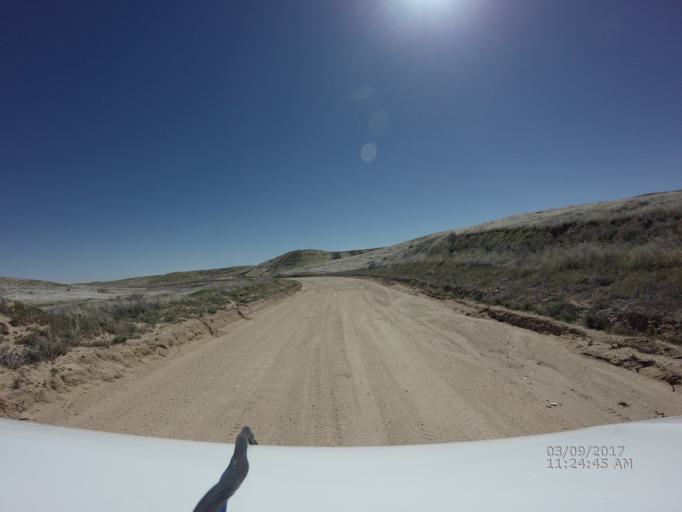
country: US
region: California
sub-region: Los Angeles County
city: Green Valley
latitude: 34.7093
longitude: -118.3980
